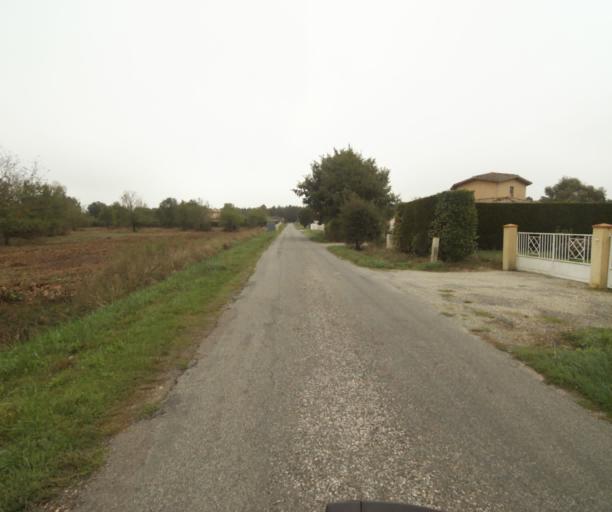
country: FR
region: Midi-Pyrenees
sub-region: Departement du Tarn-et-Garonne
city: Orgueil
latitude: 43.9027
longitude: 1.3990
